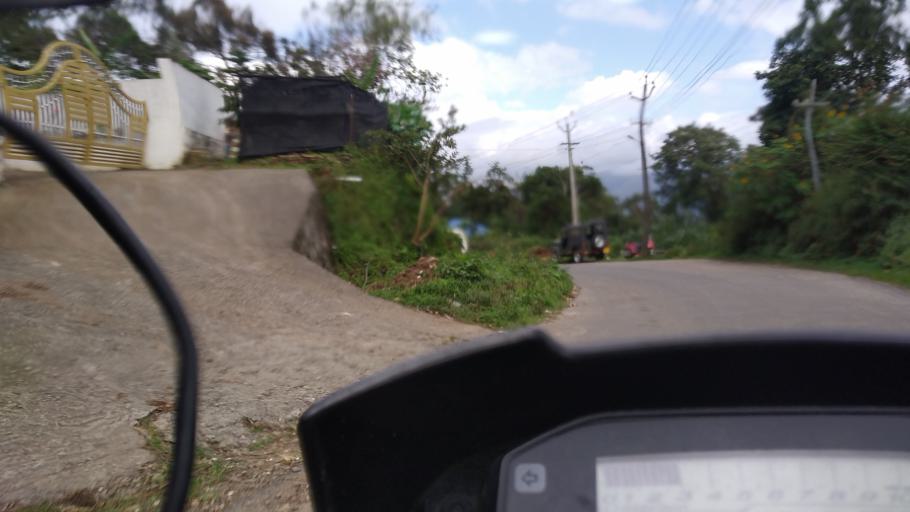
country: IN
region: Kerala
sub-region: Idukki
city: Munnar
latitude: 10.0412
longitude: 77.1763
